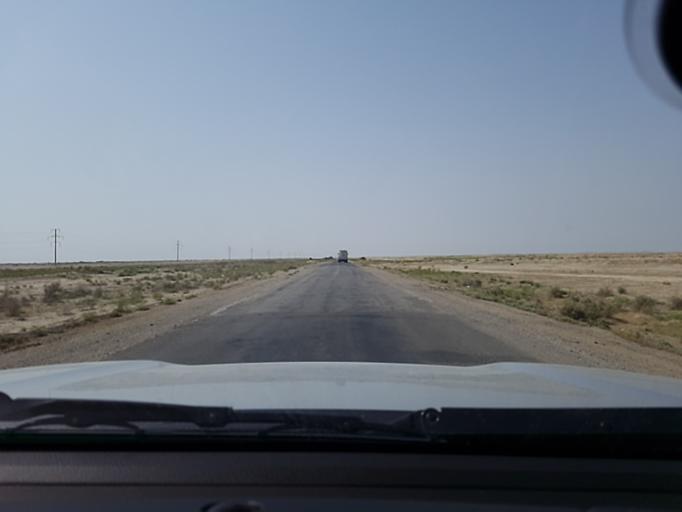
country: TM
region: Balkan
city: Gumdag
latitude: 38.8626
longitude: 54.5946
